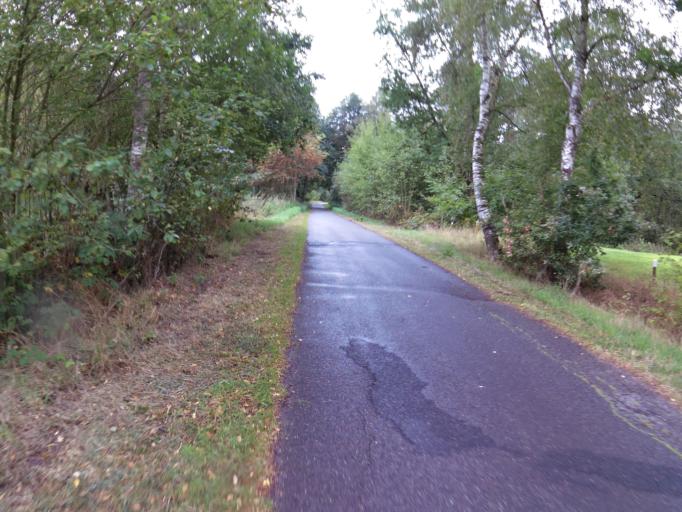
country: DE
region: Lower Saxony
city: Hamersen
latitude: 53.2693
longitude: 9.4769
